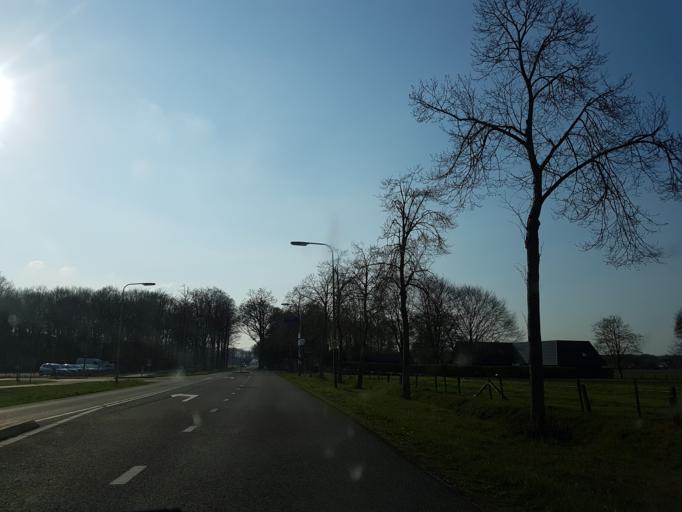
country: NL
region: Overijssel
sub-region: Gemeente Dalfsen
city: Dalfsen
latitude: 52.4980
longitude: 6.2295
